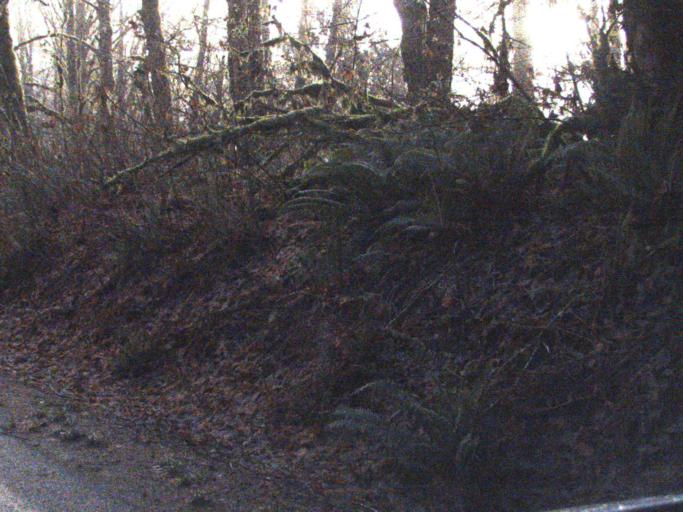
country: US
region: Washington
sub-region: Snohomish County
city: Darrington
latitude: 48.4888
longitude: -121.5816
